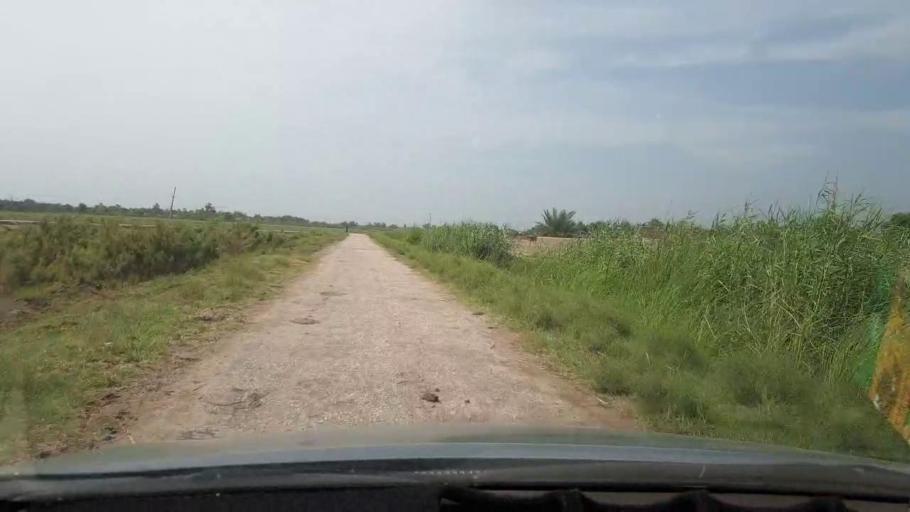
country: PK
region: Sindh
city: Khairpur
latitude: 27.4772
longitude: 68.7444
